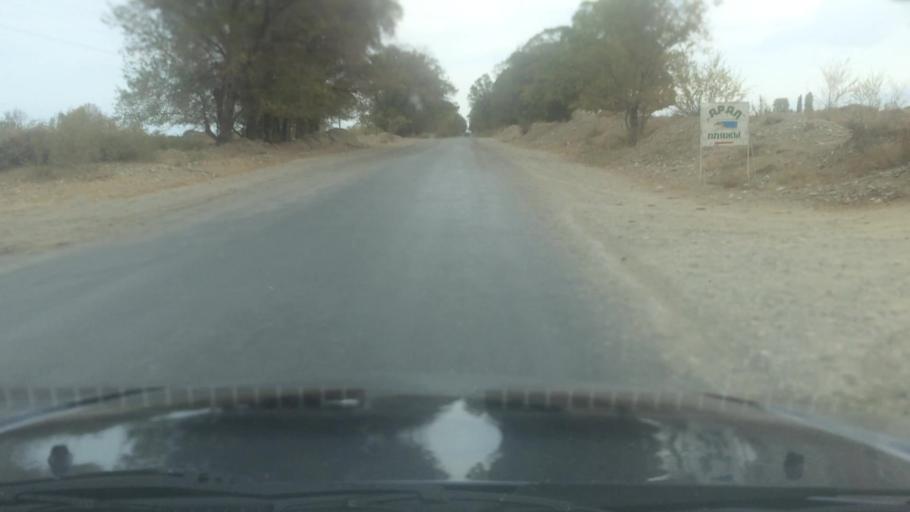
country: KG
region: Ysyk-Koel
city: Balykchy
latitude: 42.3056
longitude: 76.4718
